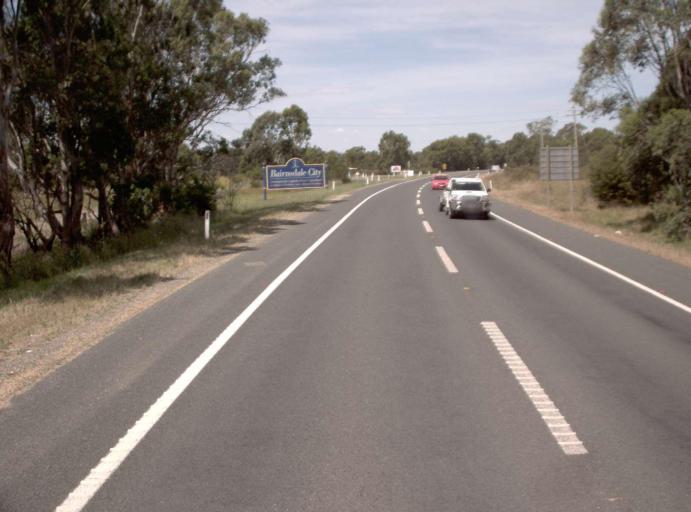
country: AU
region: Victoria
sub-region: East Gippsland
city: Bairnsdale
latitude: -37.8447
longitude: 147.5762
